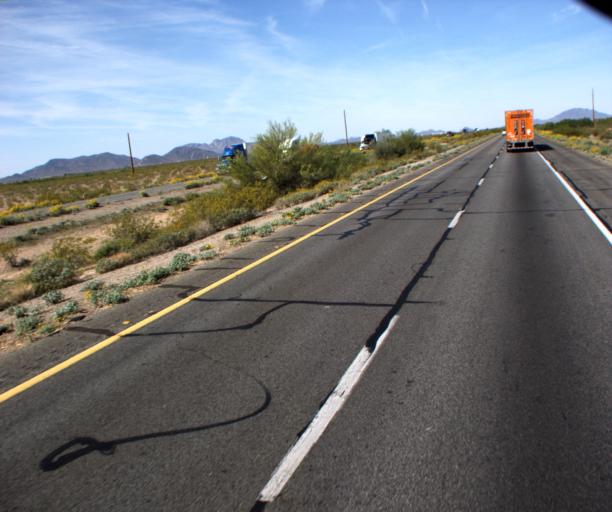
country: US
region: Arizona
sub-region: Maricopa County
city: Buckeye
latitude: 33.4738
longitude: -112.8305
